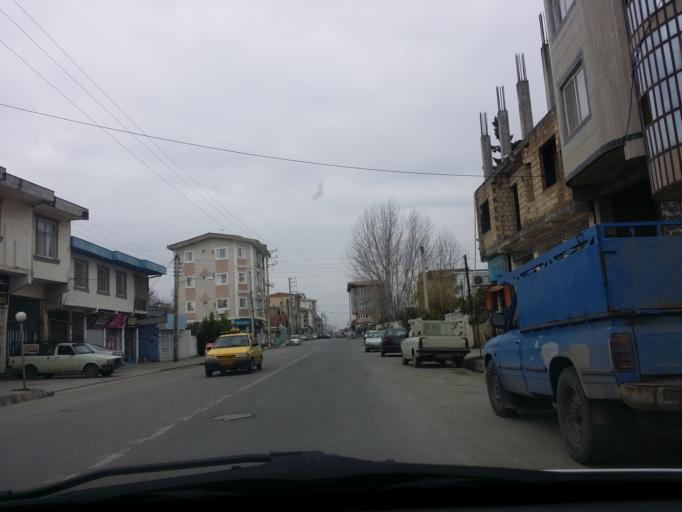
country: IR
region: Mazandaran
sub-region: Nowshahr
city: Nowshahr
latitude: 36.6422
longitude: 51.4883
